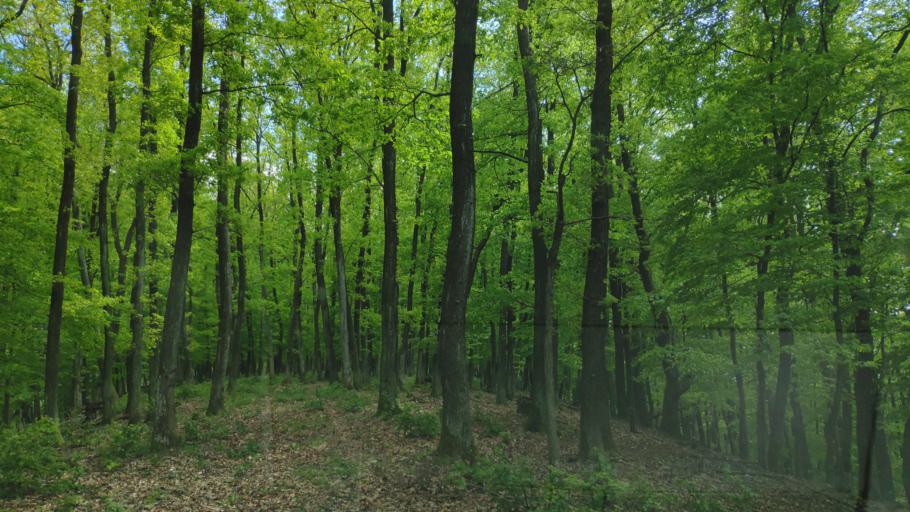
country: SK
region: Kosicky
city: Kosice
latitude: 48.6678
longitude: 21.4400
